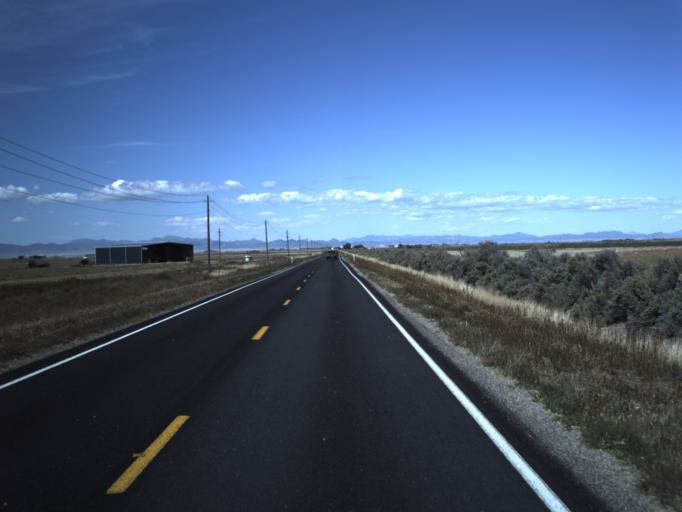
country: US
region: Utah
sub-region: Washington County
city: Enterprise
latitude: 37.6247
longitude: -113.6612
